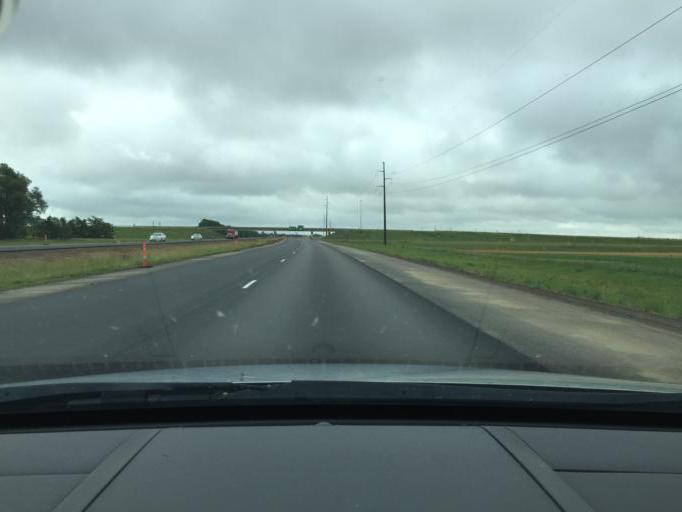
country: US
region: Kansas
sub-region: Reno County
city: South Hutchinson
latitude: 38.0131
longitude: -97.9728
